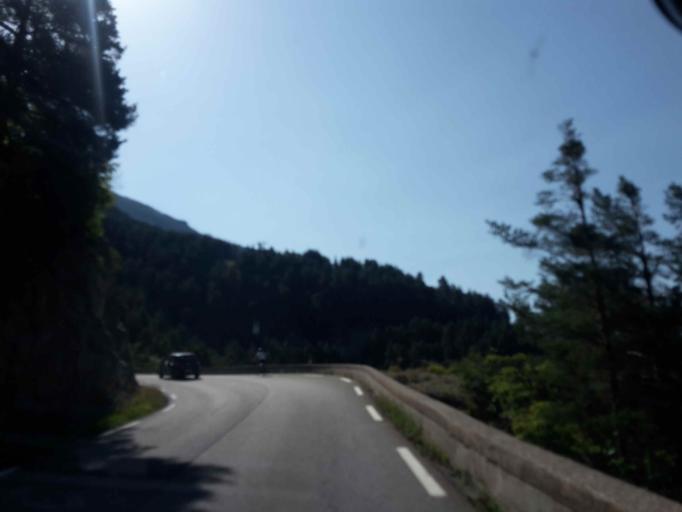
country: FR
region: Provence-Alpes-Cote d'Azur
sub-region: Departement des Hautes-Alpes
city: Guillestre
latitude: 44.6295
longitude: 6.6787
